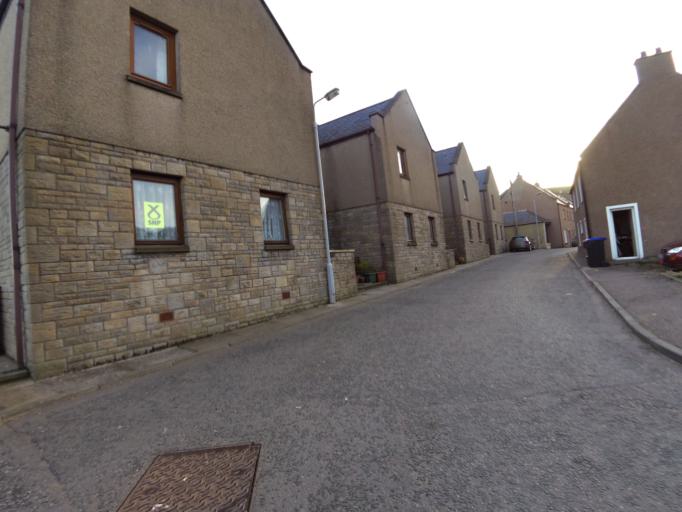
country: GB
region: Scotland
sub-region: Aberdeenshire
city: Inverbervie
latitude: 56.8280
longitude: -2.2835
